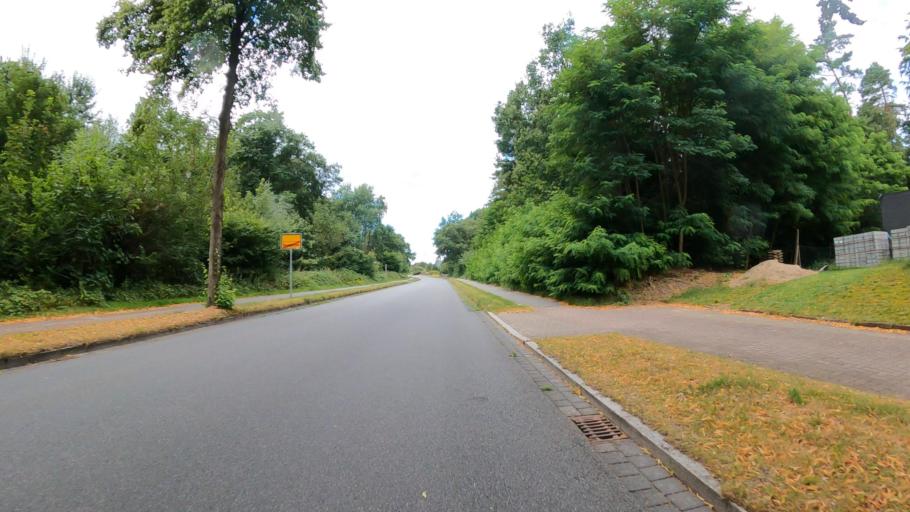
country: DE
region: Schleswig-Holstein
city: Padenstedt
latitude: 54.0568
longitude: 9.9344
